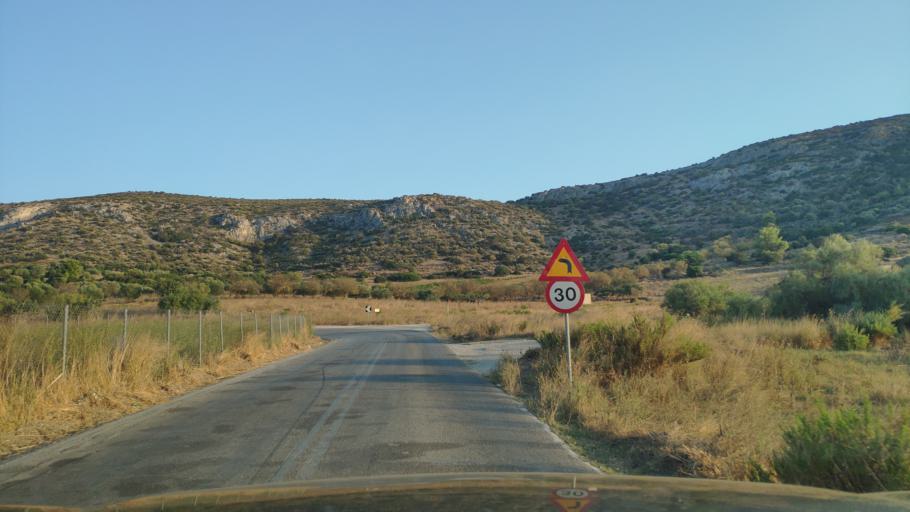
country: GR
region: Attica
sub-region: Nomarchia Anatolikis Attikis
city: Limin Mesoyaias
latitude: 37.9224
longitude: 23.9943
